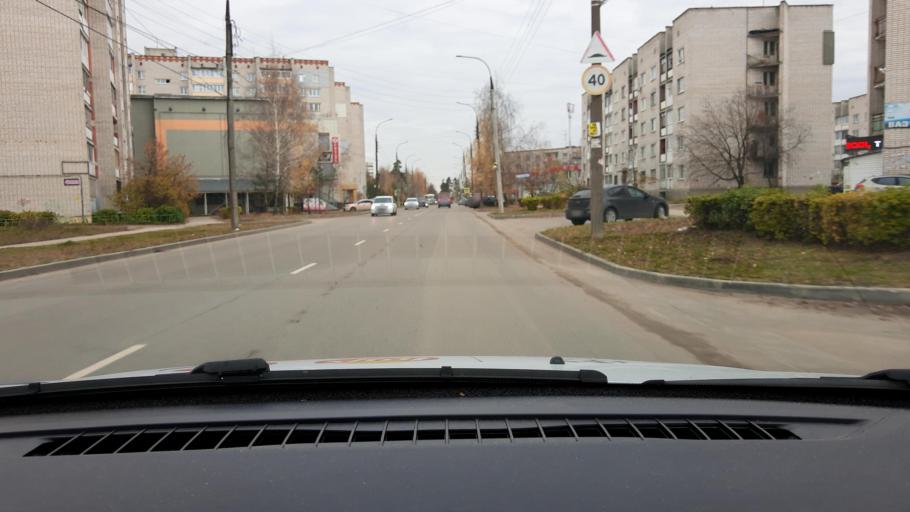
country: RU
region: Nizjnij Novgorod
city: Dzerzhinsk
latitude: 56.2547
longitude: 43.4519
